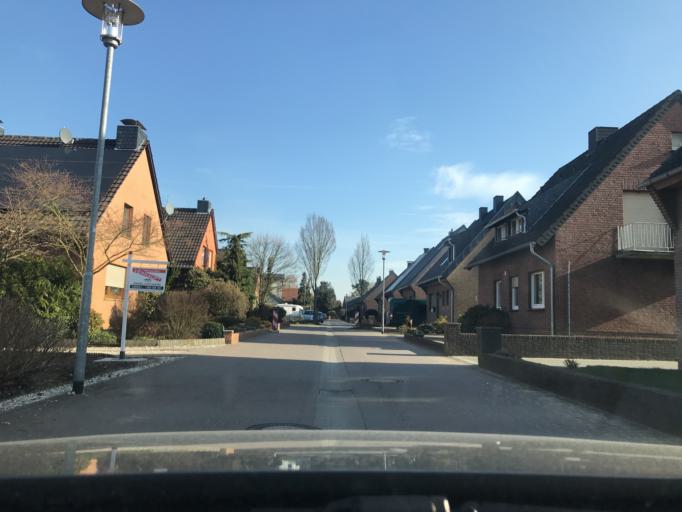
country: DE
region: North Rhine-Westphalia
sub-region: Regierungsbezirk Dusseldorf
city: Wachtendonk
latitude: 51.4024
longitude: 6.3532
